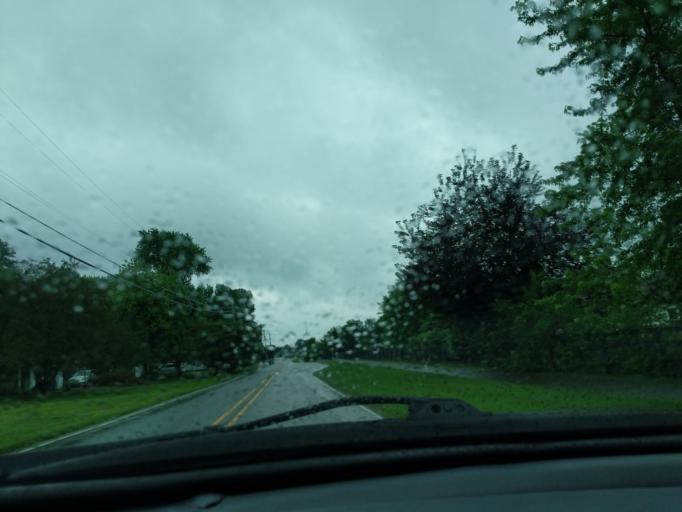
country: US
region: Indiana
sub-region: Hamilton County
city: Noblesville
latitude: 40.0725
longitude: -86.0369
